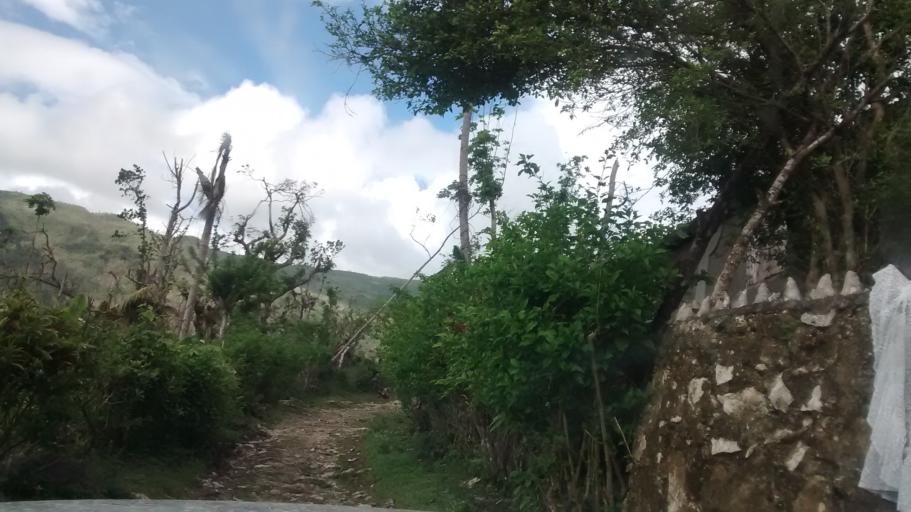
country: HT
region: Grandans
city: Moron
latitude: 18.5608
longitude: -74.2706
